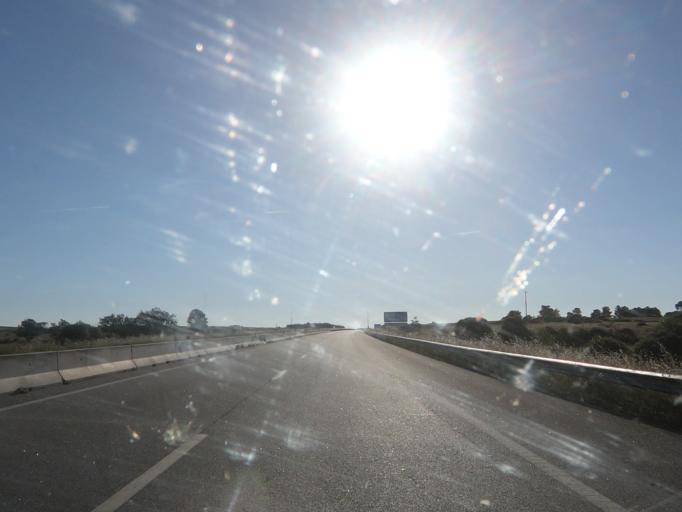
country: ES
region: Castille and Leon
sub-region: Provincia de Salamanca
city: Fuentes de Onoro
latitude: 40.6083
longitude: -6.9889
